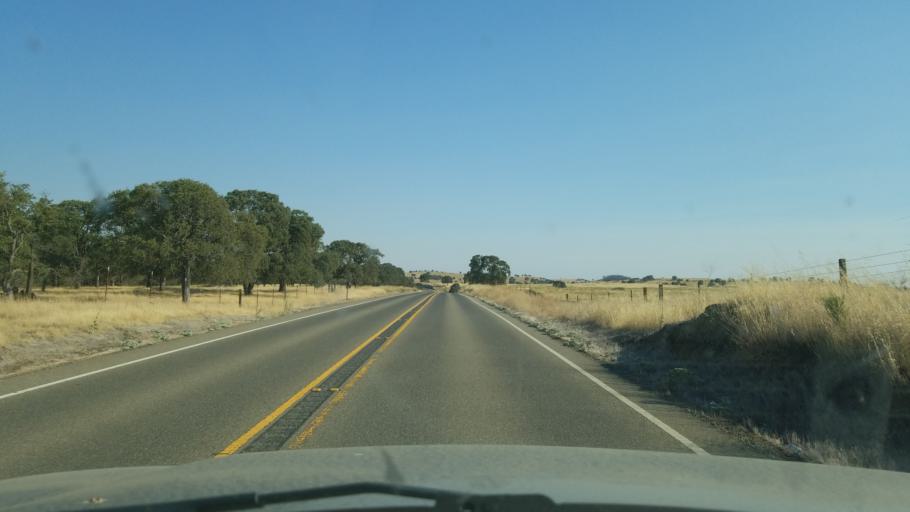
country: US
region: California
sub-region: Tuolumne County
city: Jamestown
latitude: 37.8095
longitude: -120.4728
